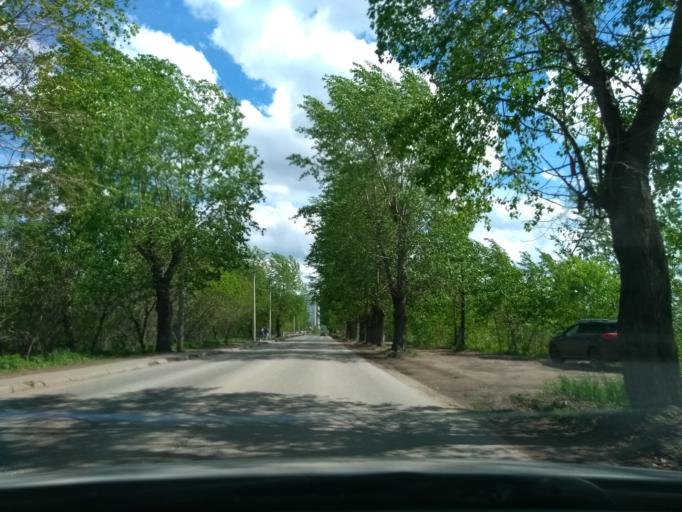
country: RU
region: Perm
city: Kondratovo
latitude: 58.0032
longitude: 56.1283
